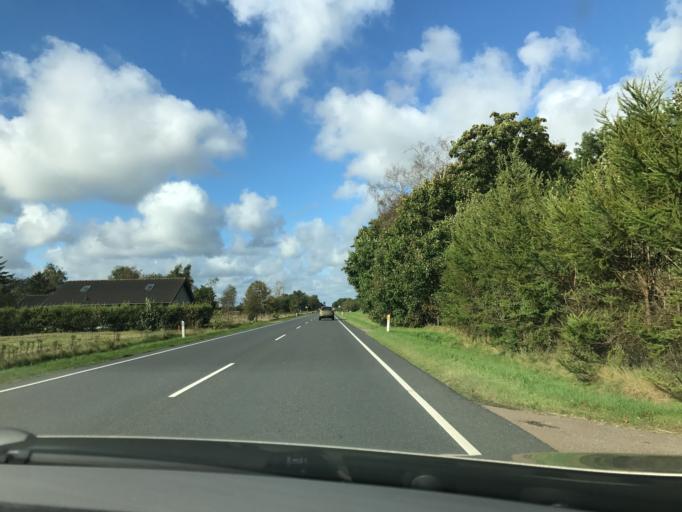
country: DK
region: South Denmark
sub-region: Billund Kommune
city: Billund
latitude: 55.7226
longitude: 9.1482
